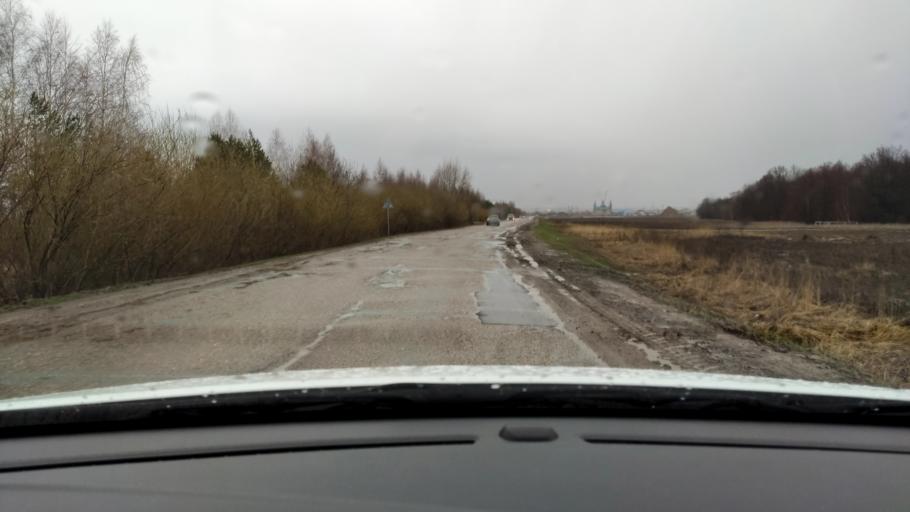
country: RU
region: Tatarstan
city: Vysokaya Gora
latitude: 55.8937
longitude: 49.3347
